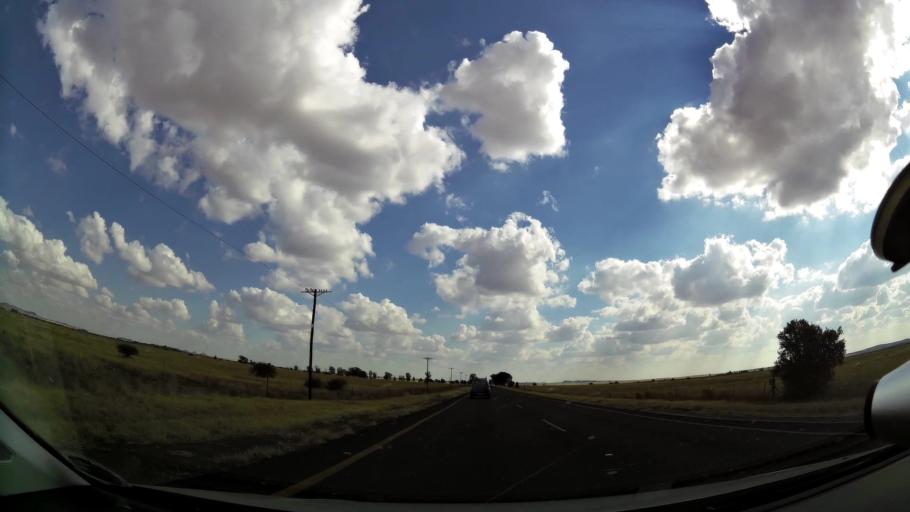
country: ZA
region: Orange Free State
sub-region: Xhariep District Municipality
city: Koffiefontein
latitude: -29.1318
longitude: 25.5343
